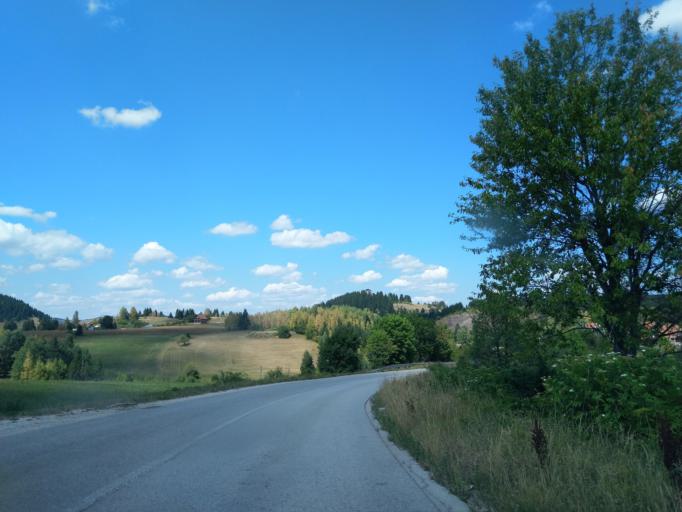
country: RS
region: Central Serbia
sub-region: Zlatiborski Okrug
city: Nova Varos
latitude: 43.4240
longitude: 19.8270
